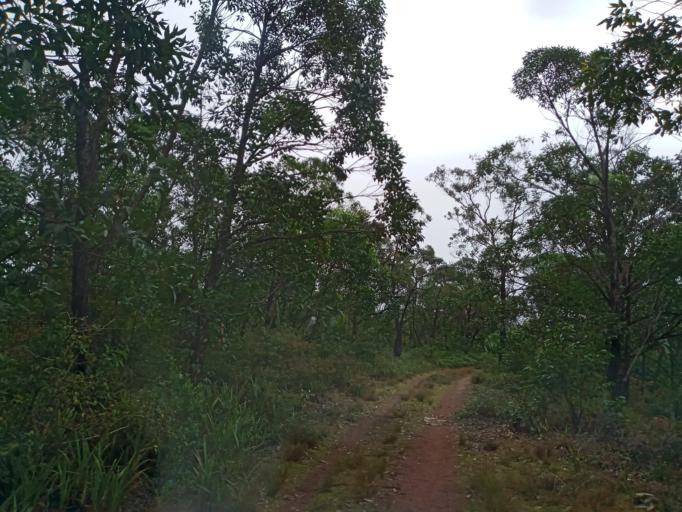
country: MG
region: Atsimo-Atsinanana
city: Vohipaho
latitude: -24.0025
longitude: 47.4040
